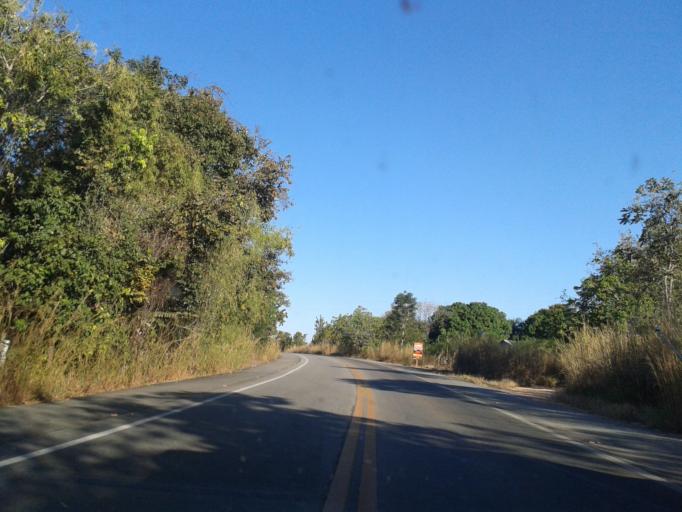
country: BR
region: Goias
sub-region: Itapuranga
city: Itapuranga
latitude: -15.5524
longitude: -50.2875
